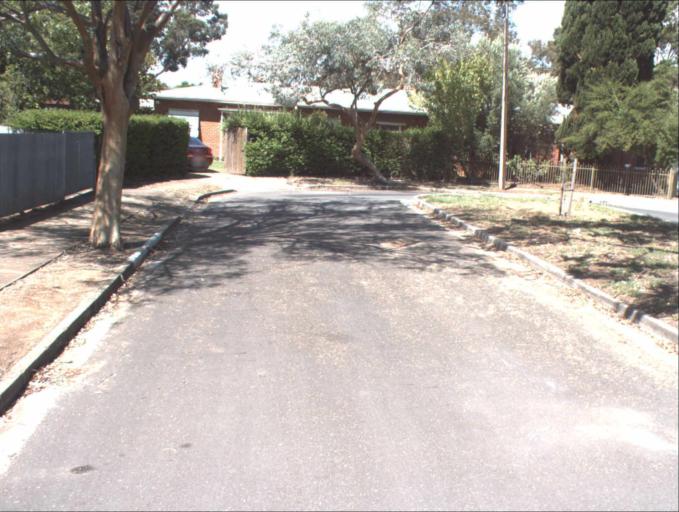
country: AU
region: South Australia
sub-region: Port Adelaide Enfield
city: Blair Athol
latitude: -34.8548
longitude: 138.5893
